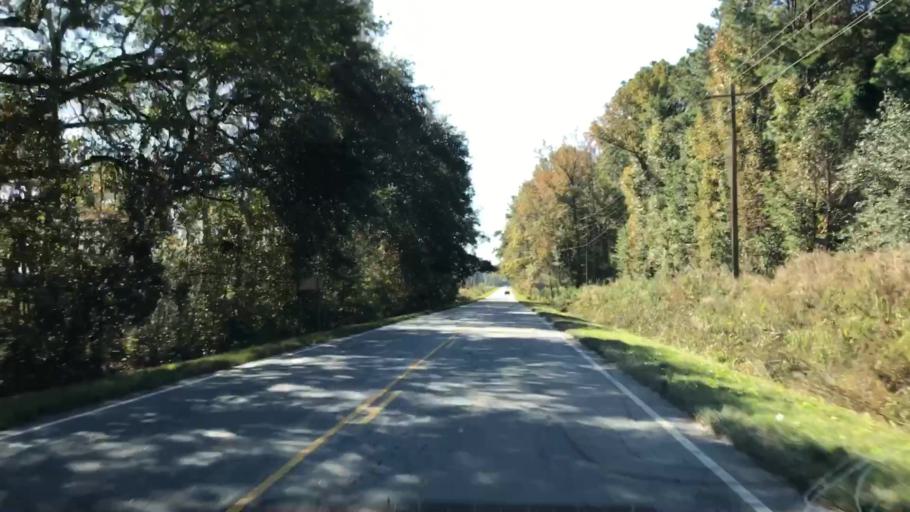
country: US
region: South Carolina
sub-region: Jasper County
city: Ridgeland
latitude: 32.4271
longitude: -80.8967
